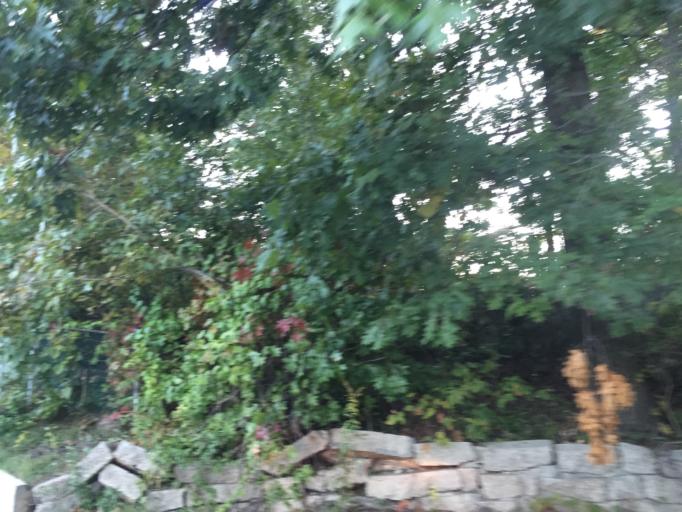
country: US
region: Maryland
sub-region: Baltimore County
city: Essex
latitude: 39.3213
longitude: -76.4778
